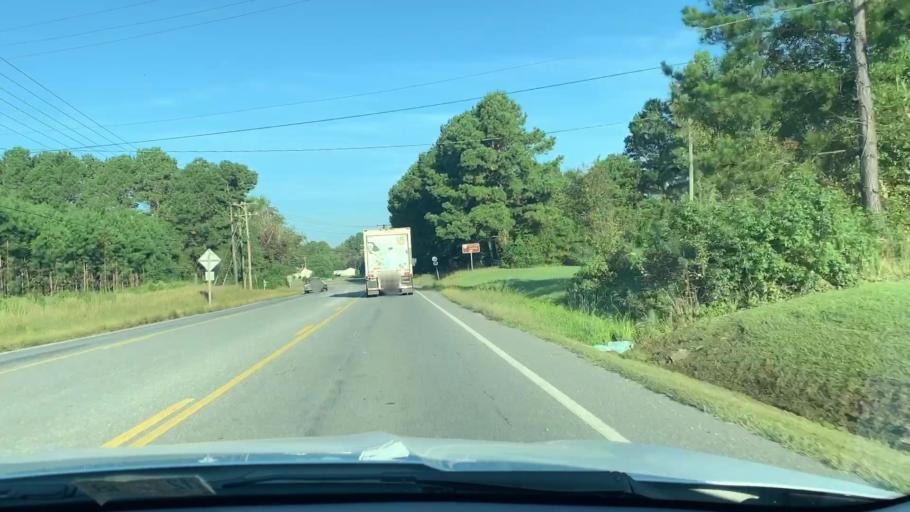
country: US
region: Virginia
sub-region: Middlesex County
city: Deltaville
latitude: 37.5534
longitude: -76.4493
